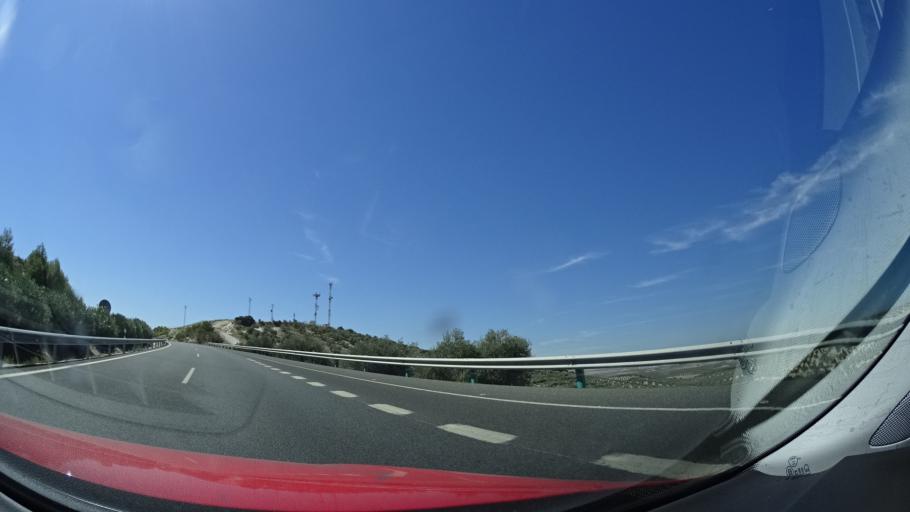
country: ES
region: Andalusia
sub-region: Provincia de Sevilla
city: Estepa
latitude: 37.2933
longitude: -4.9039
